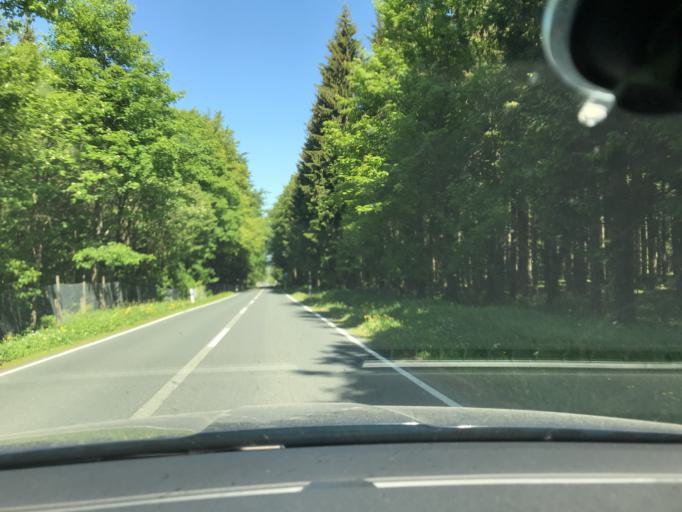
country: CZ
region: Ustecky
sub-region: Okres Chomutov
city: Vejprty
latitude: 50.4615
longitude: 12.9947
